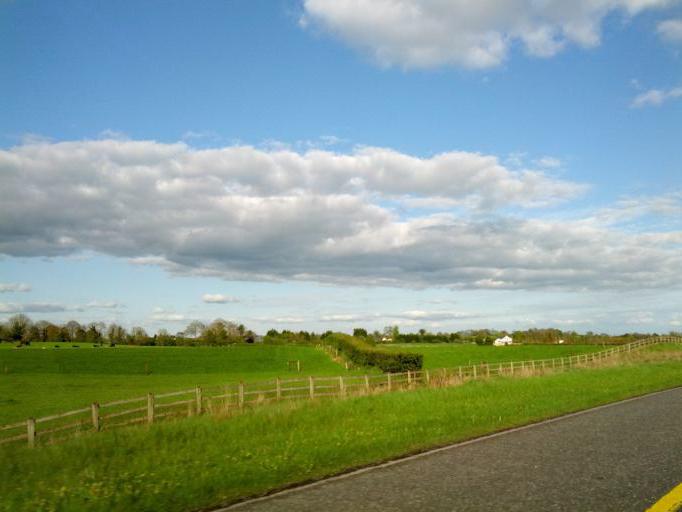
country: IE
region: Leinster
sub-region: An Mhi
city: Longwood
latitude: 53.4381
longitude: -7.0095
